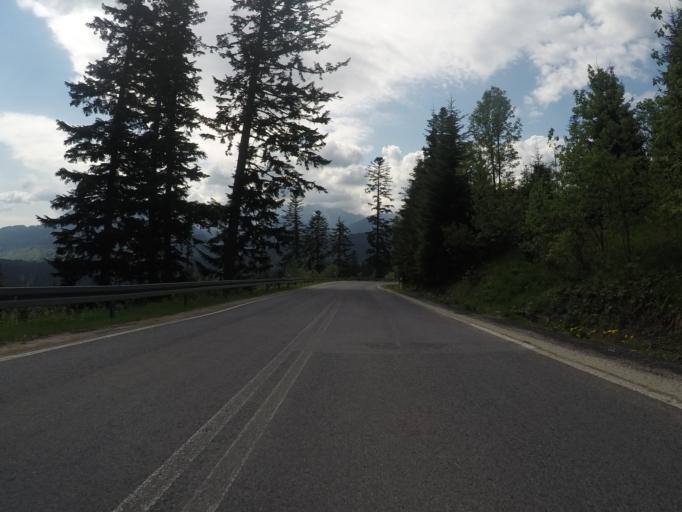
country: PL
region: Lesser Poland Voivodeship
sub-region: Powiat tatrzanski
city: Bukowina Tatrzanska
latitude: 49.2824
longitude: 20.1139
